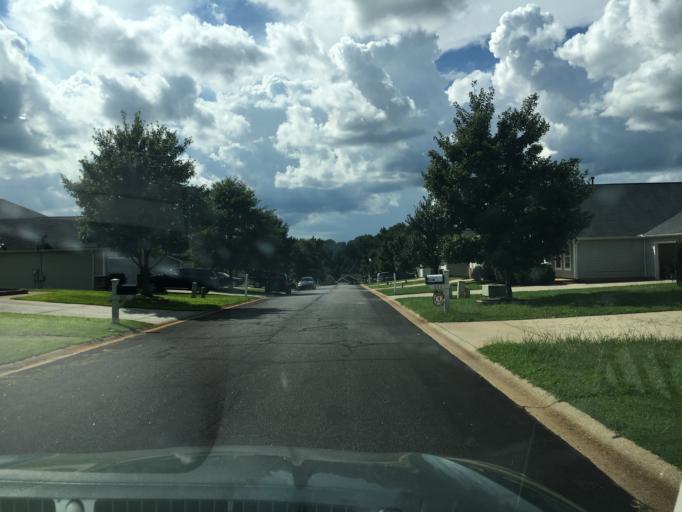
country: US
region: South Carolina
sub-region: Spartanburg County
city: Valley Falls
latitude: 35.0064
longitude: -81.9922
